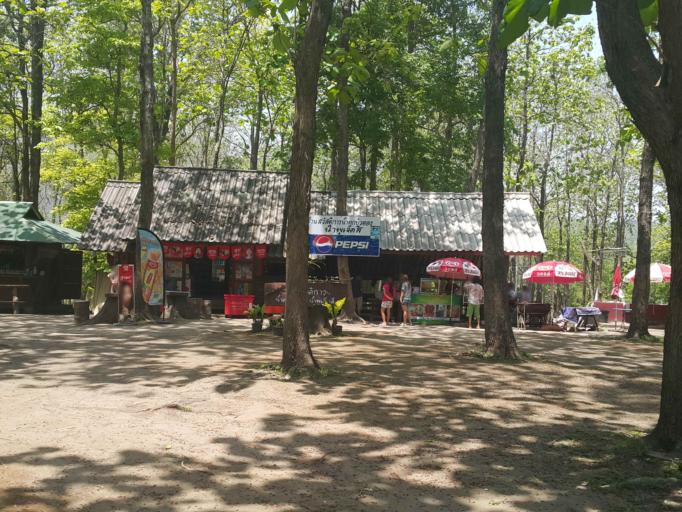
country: TH
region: Chiang Mai
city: Mae Taeng
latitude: 19.0691
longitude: 99.0794
